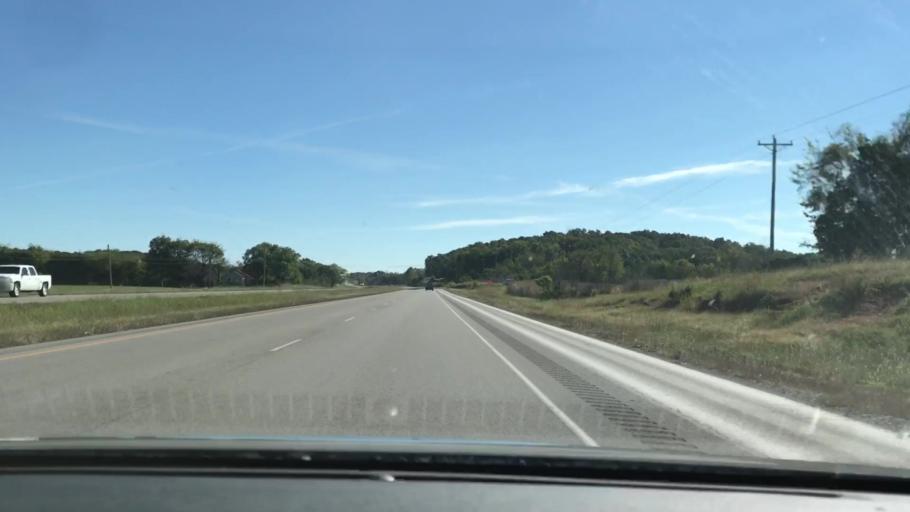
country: US
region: Kentucky
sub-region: Christian County
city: Hopkinsville
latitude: 36.8483
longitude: -87.3355
